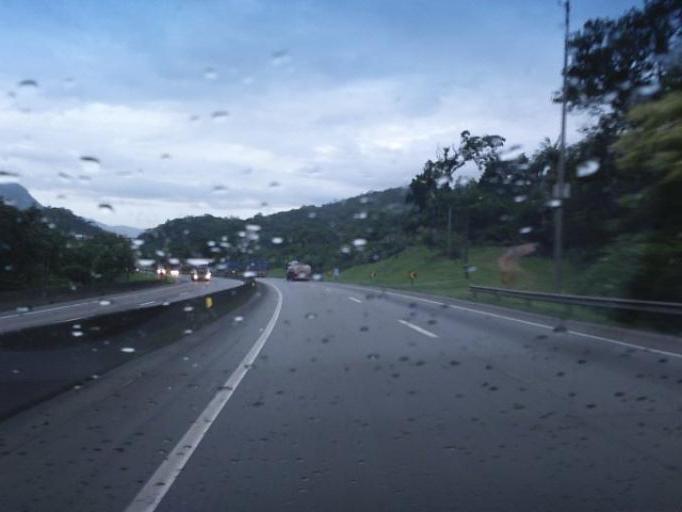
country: BR
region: Parana
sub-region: Guaratuba
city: Guaratuba
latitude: -25.9487
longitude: -48.9065
